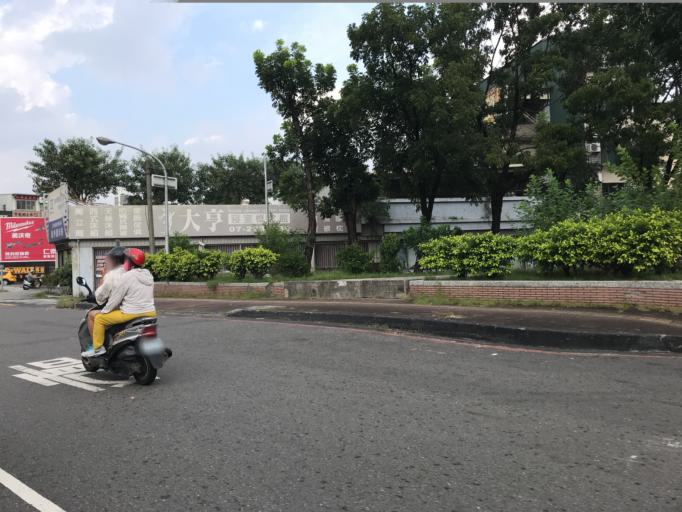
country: TW
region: Kaohsiung
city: Kaohsiung
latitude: 22.6363
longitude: 120.3139
